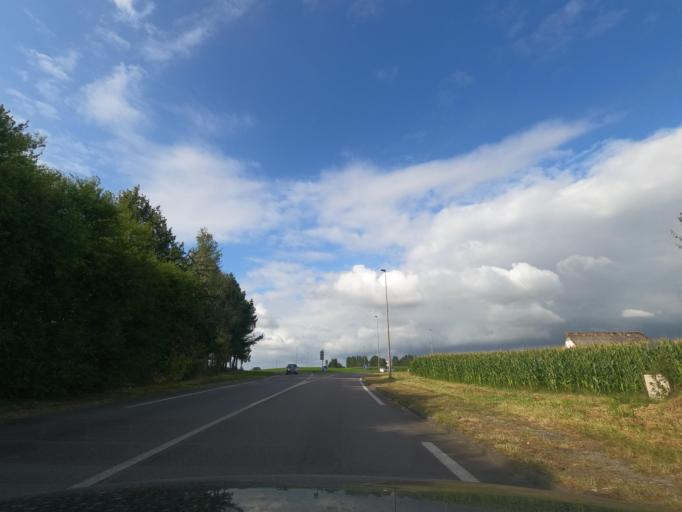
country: FR
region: Haute-Normandie
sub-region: Departement de l'Eure
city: Bernay
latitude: 49.0947
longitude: 0.5750
